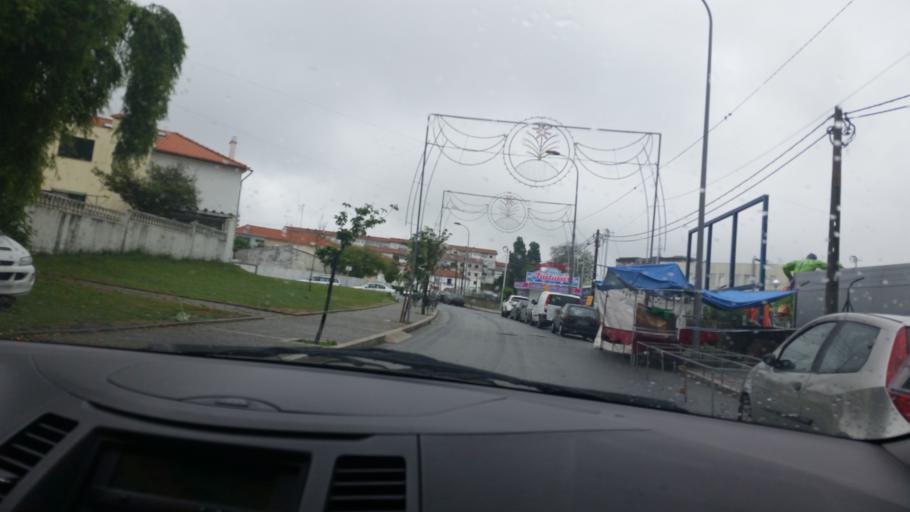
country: PT
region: Porto
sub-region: Matosinhos
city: Matosinhos
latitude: 41.1872
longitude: -8.6820
